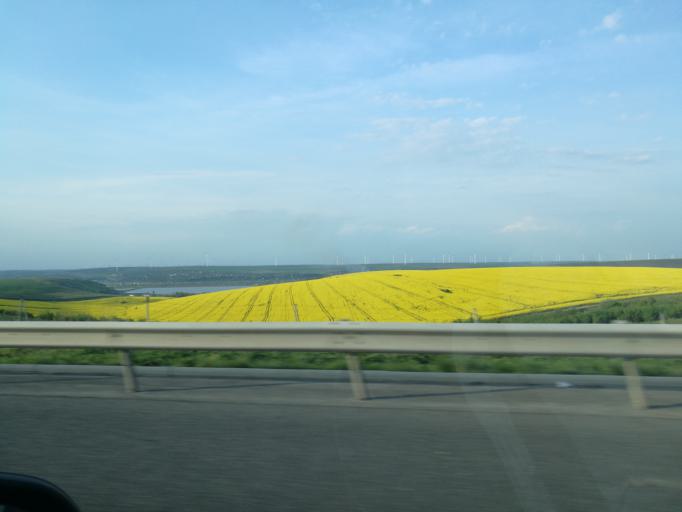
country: RO
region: Constanta
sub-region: Comuna Saligny
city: Saligny
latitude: 44.2467
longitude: 28.0848
